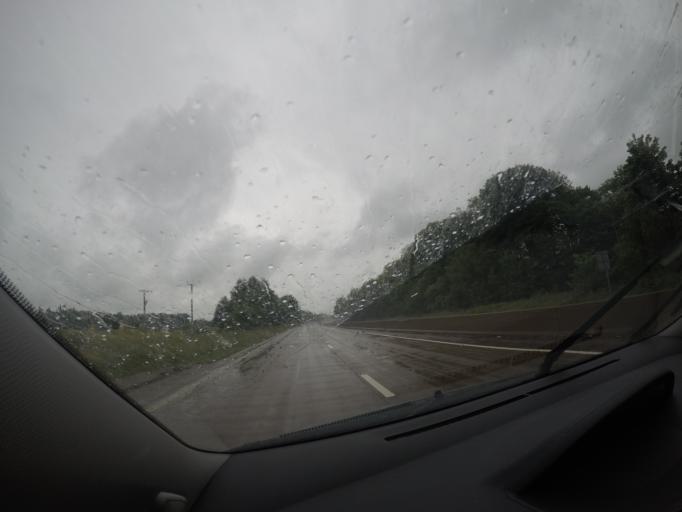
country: GB
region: Scotland
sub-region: Angus
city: Brechin
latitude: 56.7319
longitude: -2.6918
